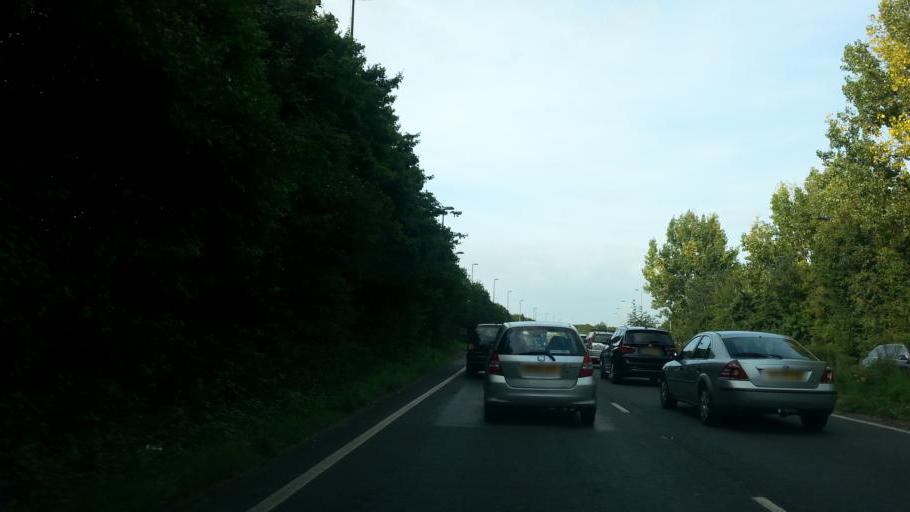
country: GB
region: England
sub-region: Hampshire
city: Eastleigh
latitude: 50.9454
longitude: -1.3731
